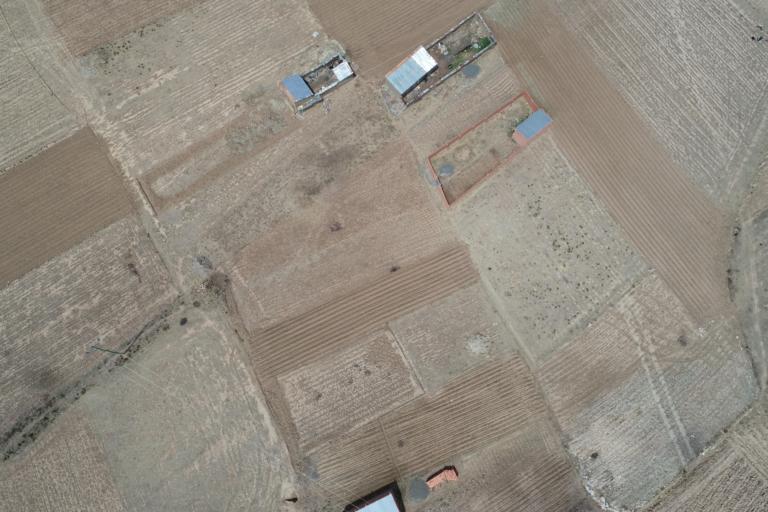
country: BO
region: La Paz
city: Achacachi
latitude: -16.0536
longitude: -68.6754
